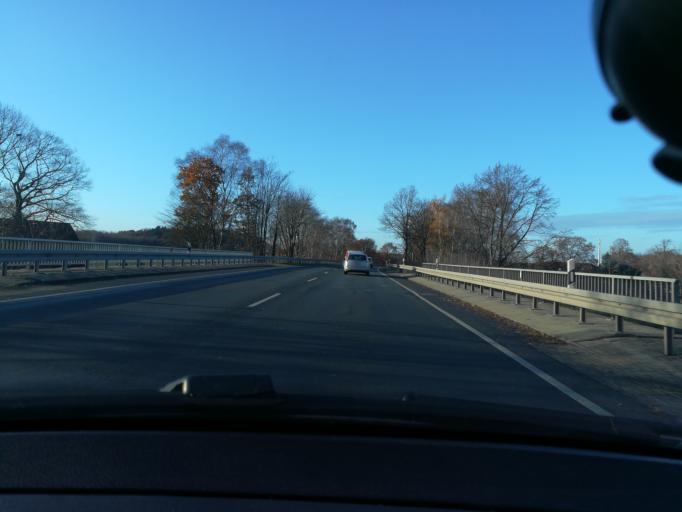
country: DE
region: Lower Saxony
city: Kirchdorf
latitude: 52.5925
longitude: 8.8333
